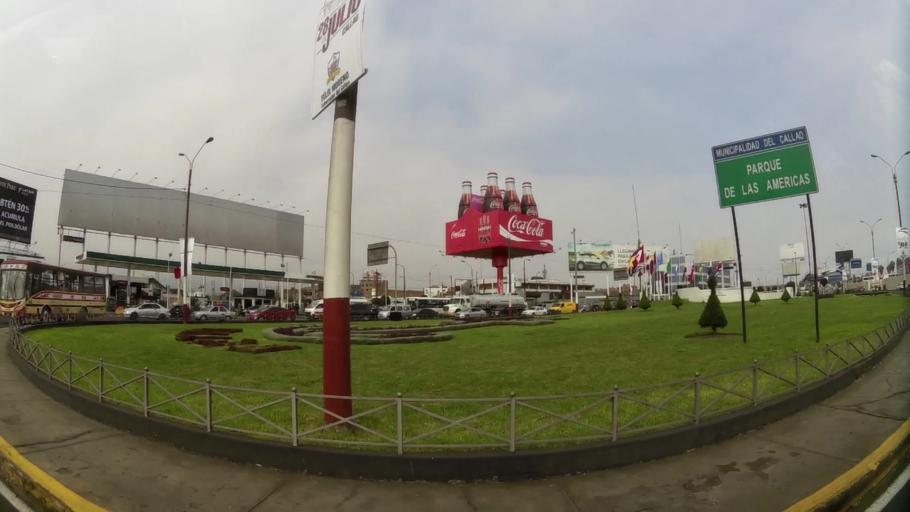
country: PE
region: Callao
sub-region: Callao
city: Callao
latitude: -12.0215
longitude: -77.1065
